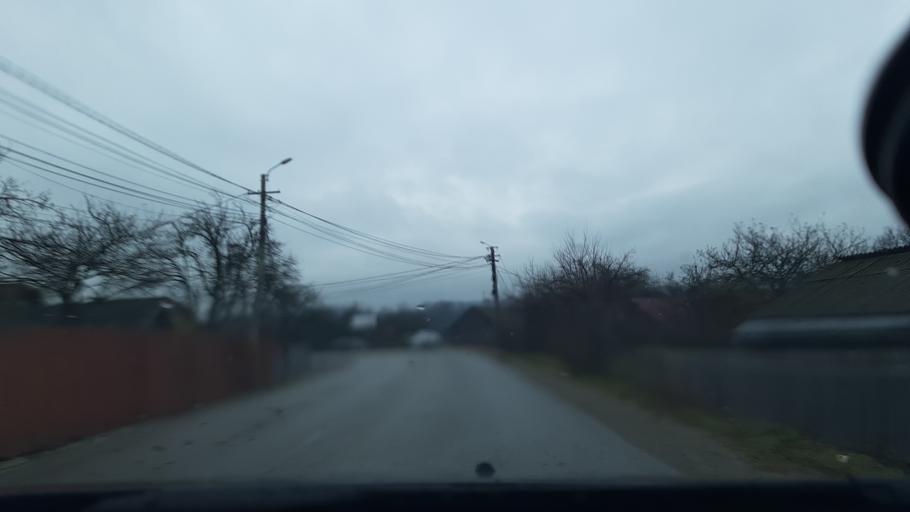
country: RO
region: Hunedoara
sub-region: Oras Petrila
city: Petrila
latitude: 45.4411
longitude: 23.4116
